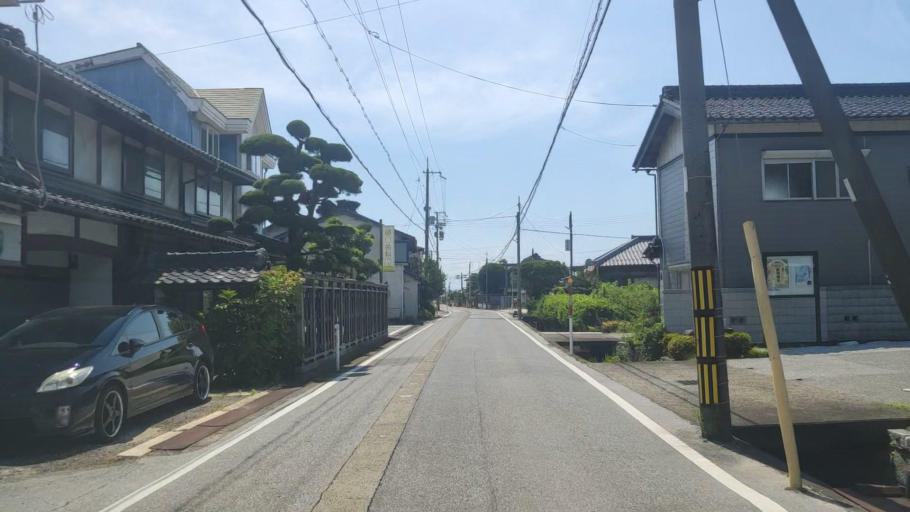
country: JP
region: Shiga Prefecture
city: Nagahama
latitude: 35.3875
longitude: 136.3128
